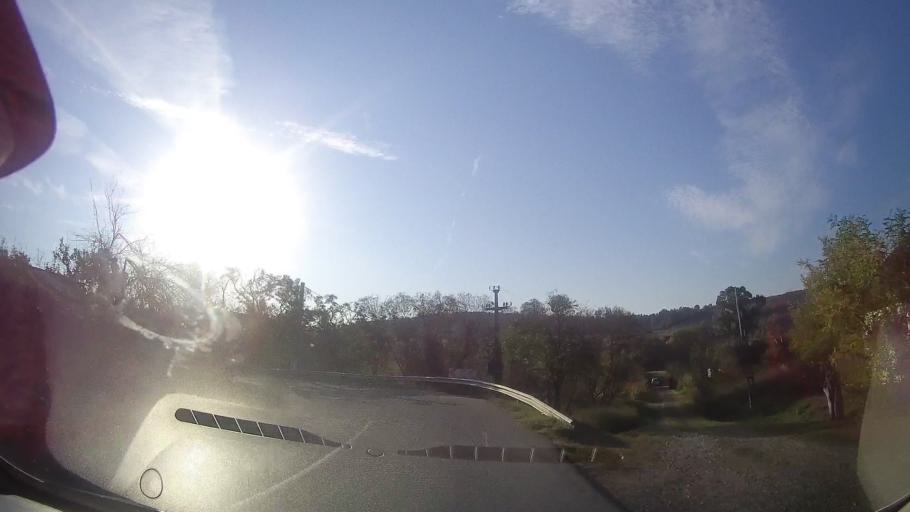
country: RO
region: Timis
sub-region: Comuna Bogda
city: Bogda
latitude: 45.9818
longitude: 21.5504
